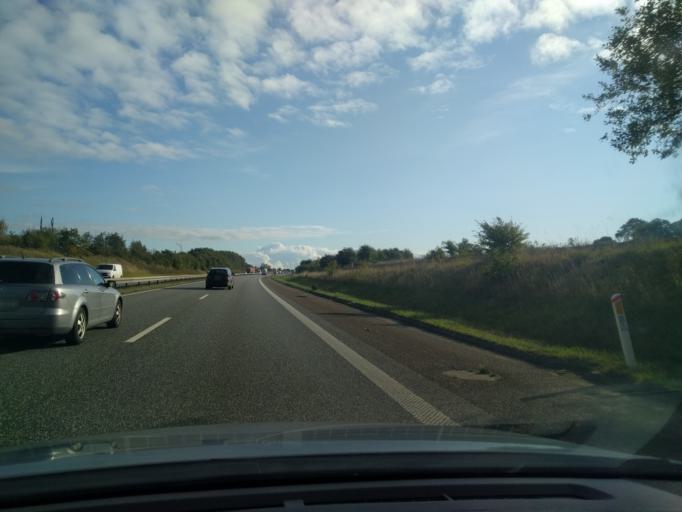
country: DK
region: Zealand
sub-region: Soro Kommune
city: Soro
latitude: 55.4500
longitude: 11.5685
